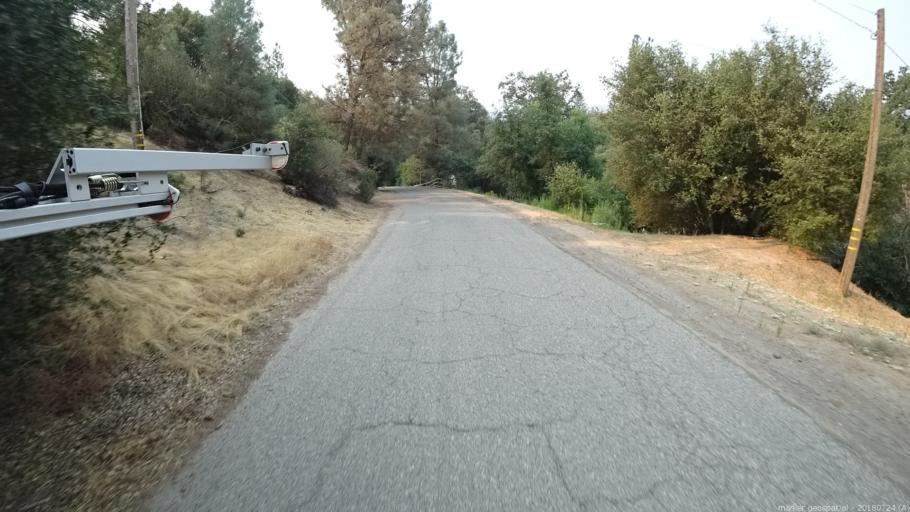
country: US
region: California
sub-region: Madera County
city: Oakhurst
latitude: 37.3248
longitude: -119.6427
